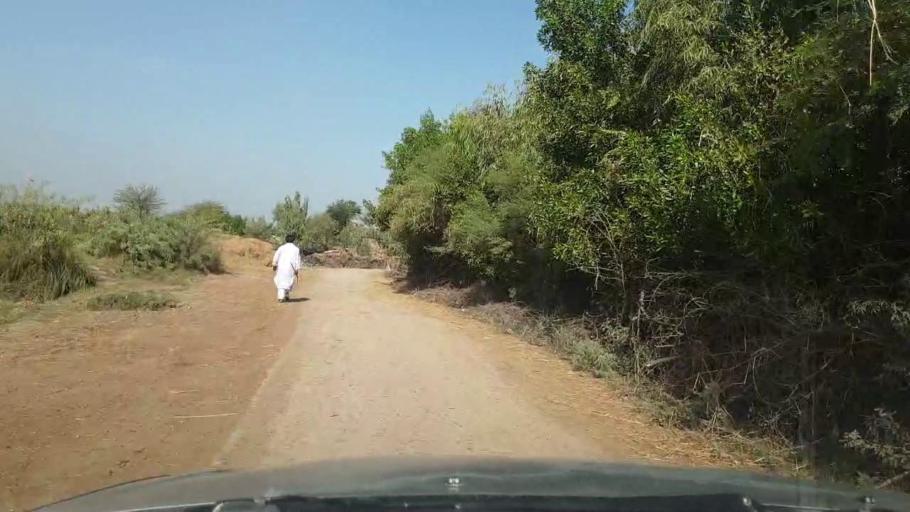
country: PK
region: Sindh
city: Tando Muhammad Khan
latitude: 25.1404
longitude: 68.5355
